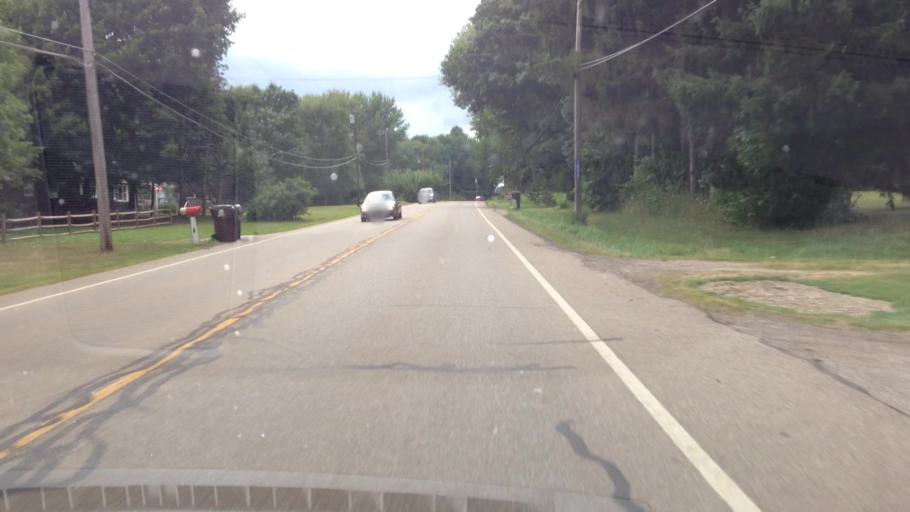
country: US
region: Ohio
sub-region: Summit County
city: Green
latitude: 40.9739
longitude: -81.4584
